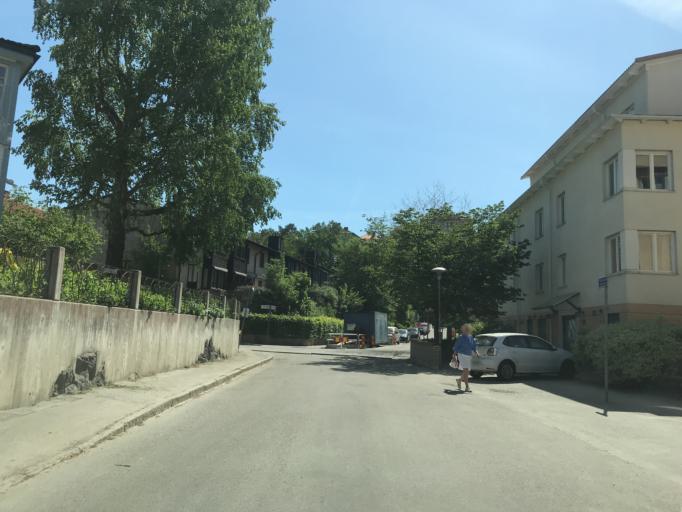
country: SE
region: Stockholm
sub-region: Solna Kommun
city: Solna
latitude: 59.3233
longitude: 17.9886
